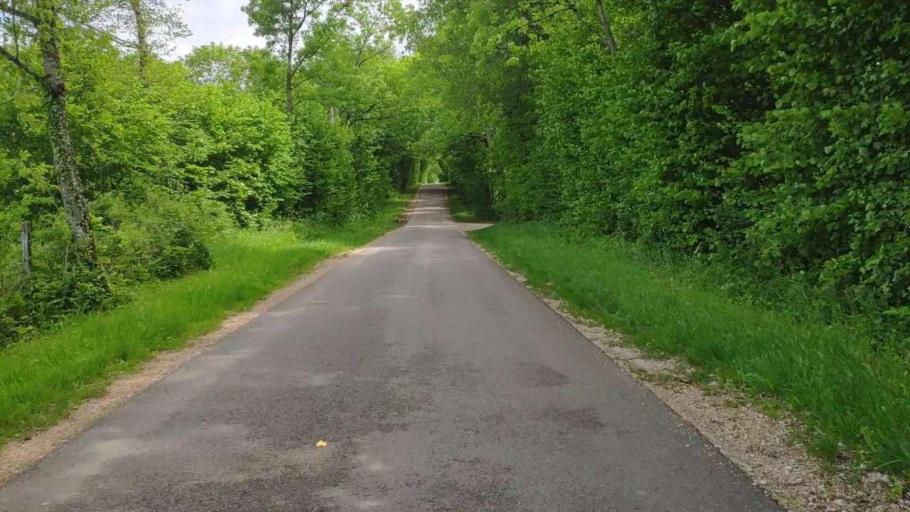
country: FR
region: Franche-Comte
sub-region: Departement du Jura
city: Poligny
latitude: 46.7848
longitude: 5.6675
